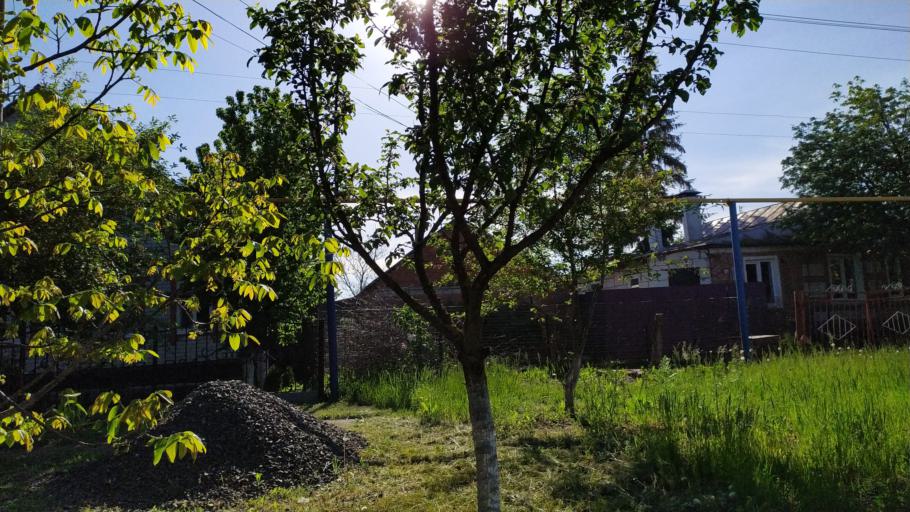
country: RU
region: Kursk
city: Kursk
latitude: 51.6383
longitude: 36.1489
